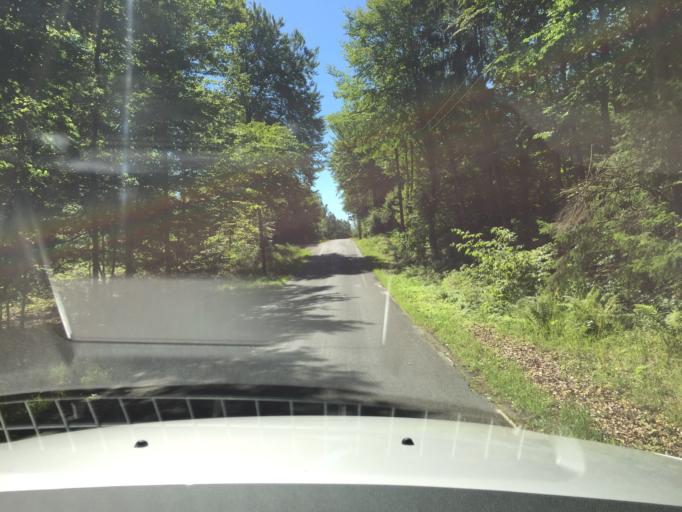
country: SE
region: Skane
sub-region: Hassleholms Kommun
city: Sosdala
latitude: 56.0088
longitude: 13.6122
